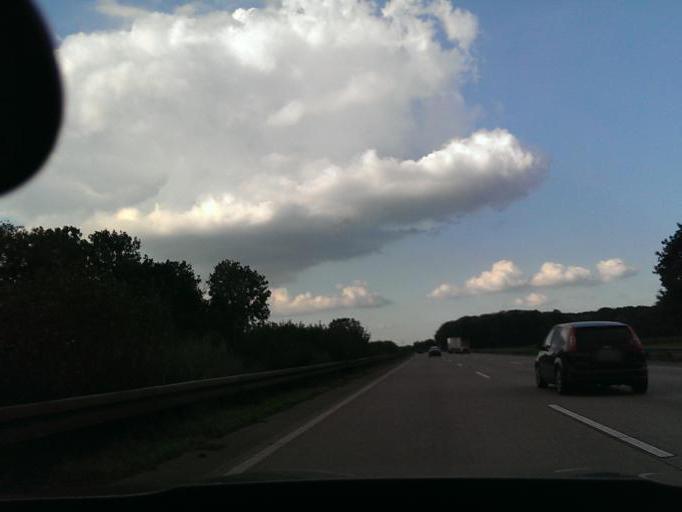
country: DE
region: Lower Saxony
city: Harsum
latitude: 52.2233
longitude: 9.9338
